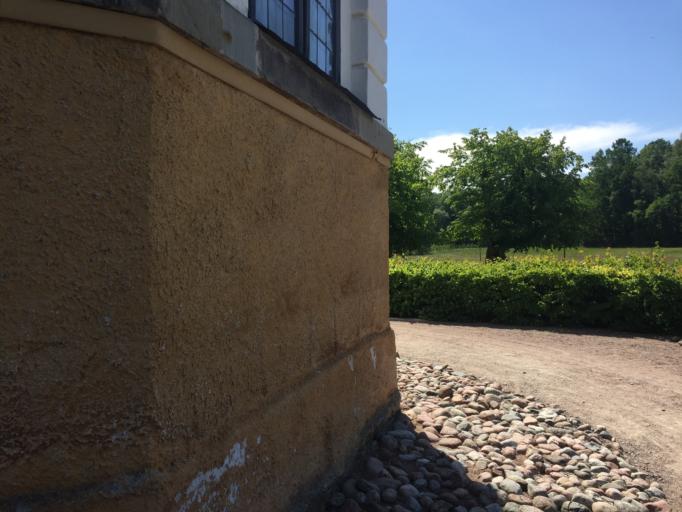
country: SE
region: Stockholm
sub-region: Sigtuna Kommun
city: Sigtuna
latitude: 59.7030
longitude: 17.6208
